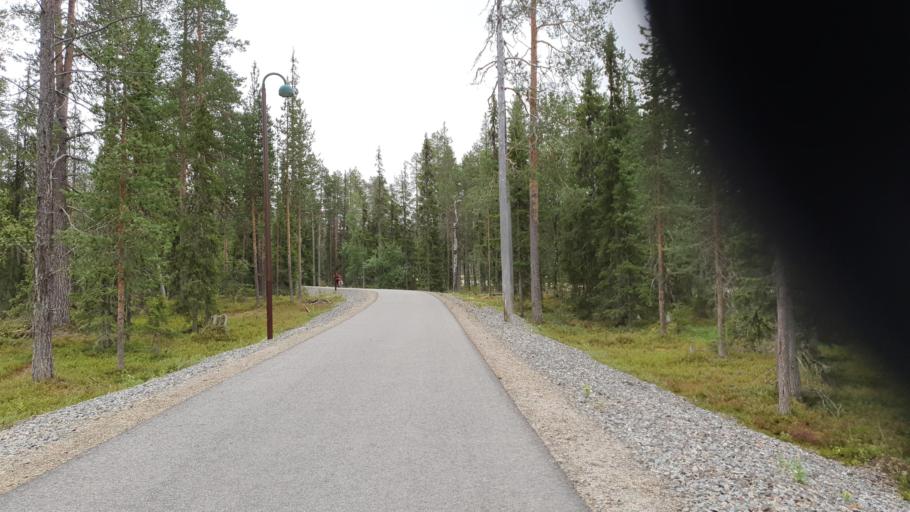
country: FI
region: Lapland
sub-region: Tunturi-Lappi
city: Kolari
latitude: 67.5964
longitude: 24.1815
